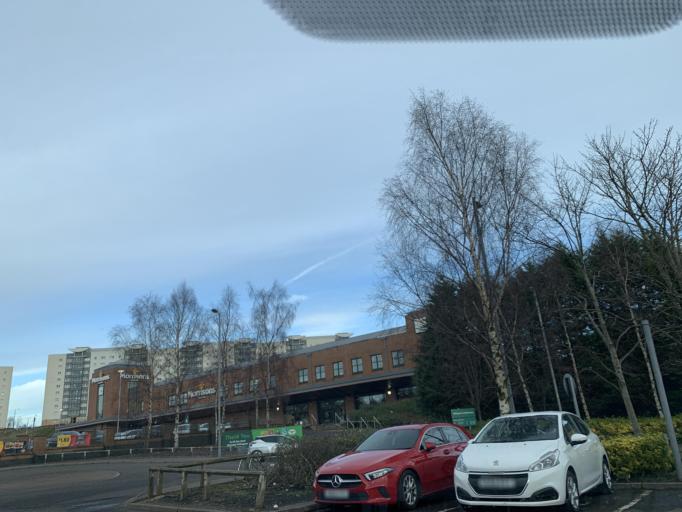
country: GB
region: Scotland
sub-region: Renfrewshire
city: Renfrew
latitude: 55.8459
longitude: -4.3425
